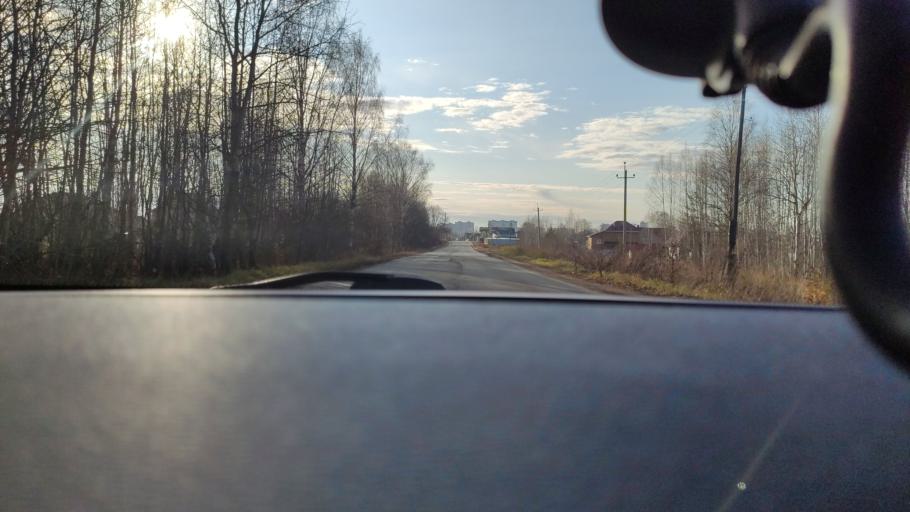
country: RU
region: Perm
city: Kondratovo
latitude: 58.0569
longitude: 56.0276
